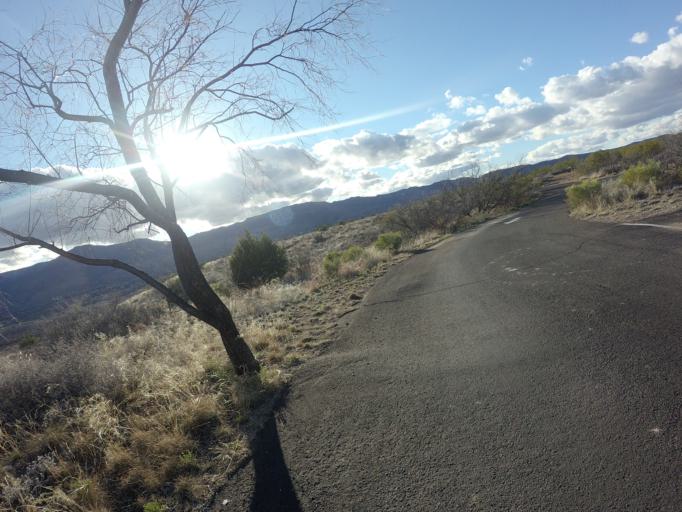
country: US
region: Arizona
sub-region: Yavapai County
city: Cottonwood
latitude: 34.7615
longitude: -112.0175
